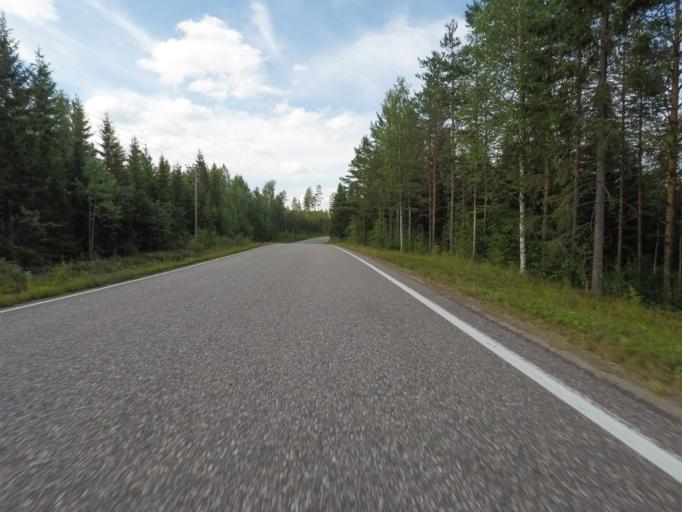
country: FI
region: Southern Savonia
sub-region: Savonlinna
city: Sulkava
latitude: 61.7447
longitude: 28.1993
